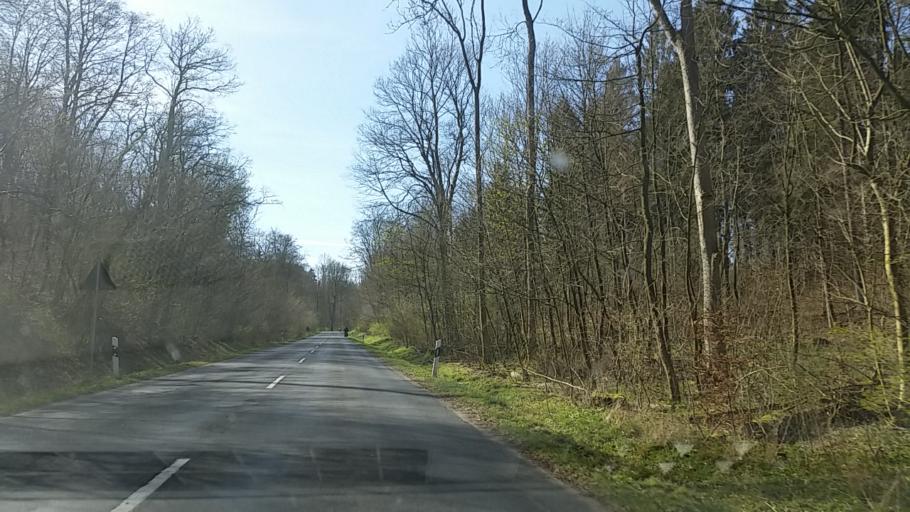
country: DE
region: Lower Saxony
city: Konigslutter am Elm
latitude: 52.2106
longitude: 10.8025
